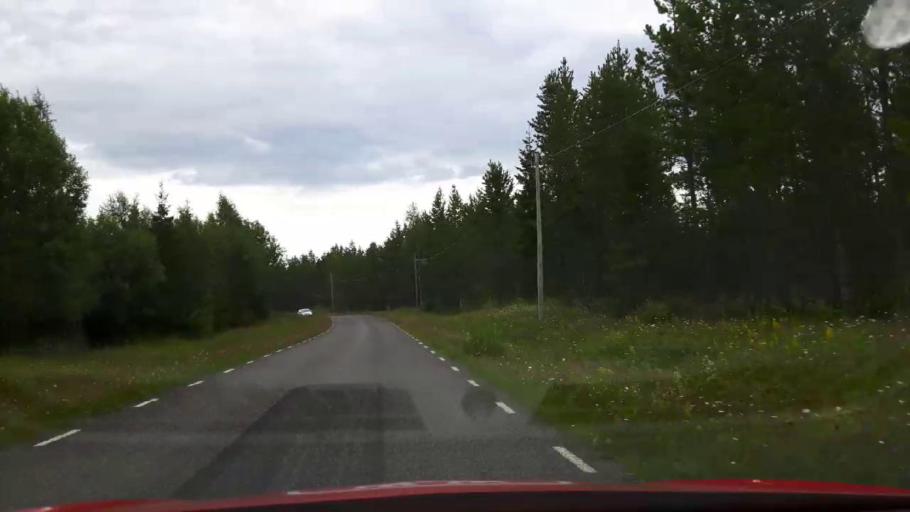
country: SE
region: Jaemtland
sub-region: OEstersunds Kommun
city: Lit
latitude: 63.3820
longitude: 15.0456
